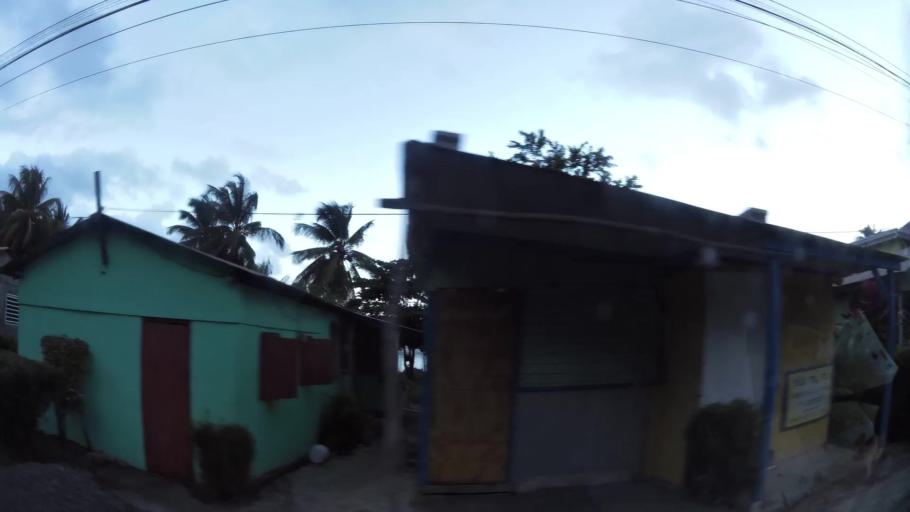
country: DM
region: Saint Andrew
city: Calibishie
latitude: 15.5925
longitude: -61.3522
